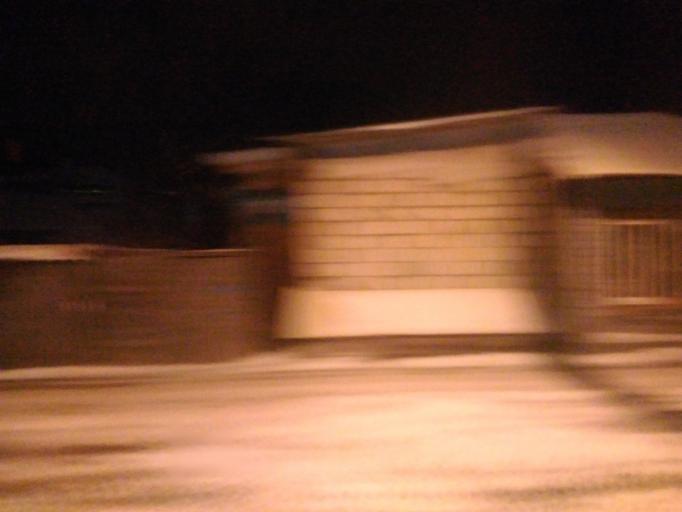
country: RU
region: Ulyanovsk
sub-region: Ulyanovskiy Rayon
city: Ulyanovsk
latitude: 54.3328
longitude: 48.4002
